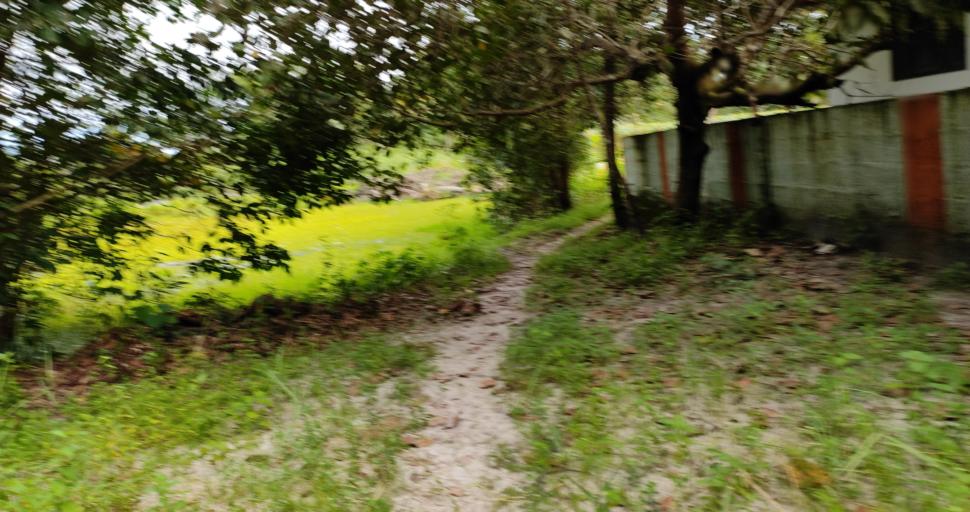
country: IN
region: Kerala
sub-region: Alappuzha
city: Shertallai
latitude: 9.6503
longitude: 76.3194
